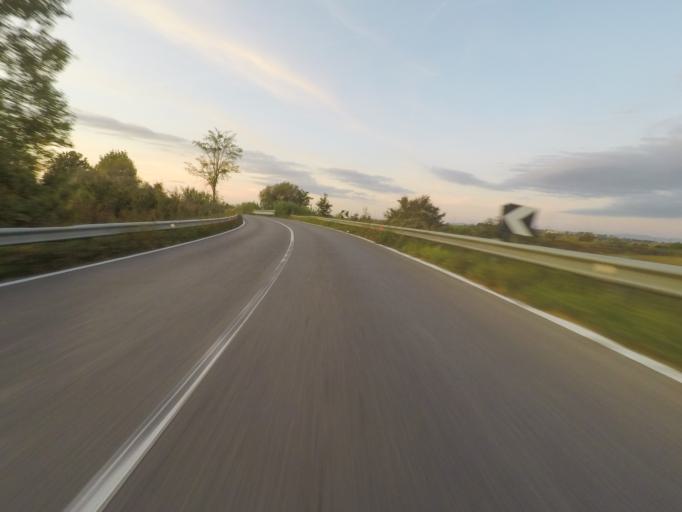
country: IT
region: Tuscany
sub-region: Provincia di Siena
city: Sinalunga
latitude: 43.1960
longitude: 11.7614
